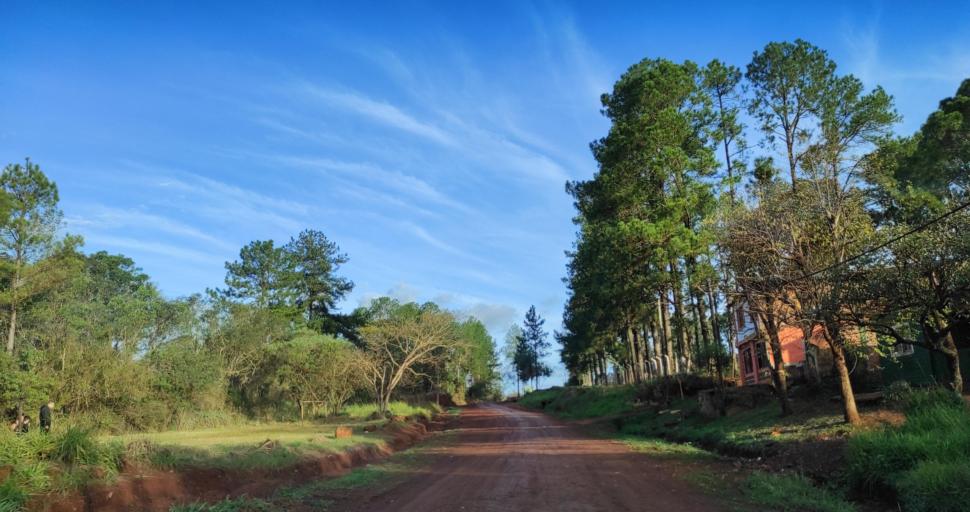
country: AR
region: Misiones
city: Garupa
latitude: -27.5122
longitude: -55.8546
